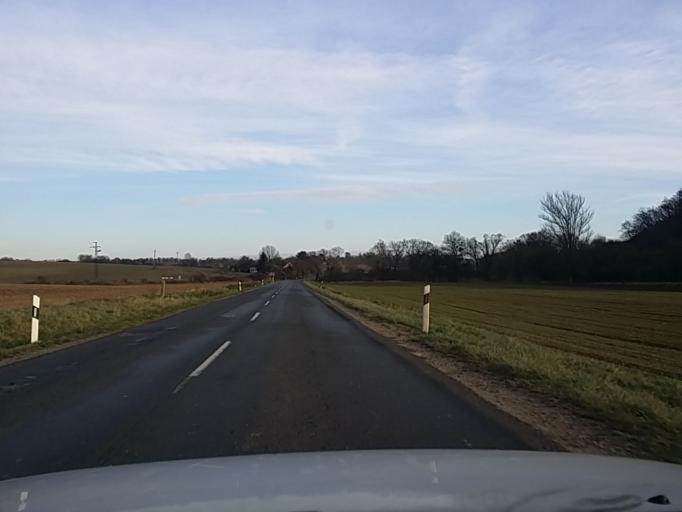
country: HU
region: Veszprem
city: Urkut
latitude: 46.9909
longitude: 17.6825
